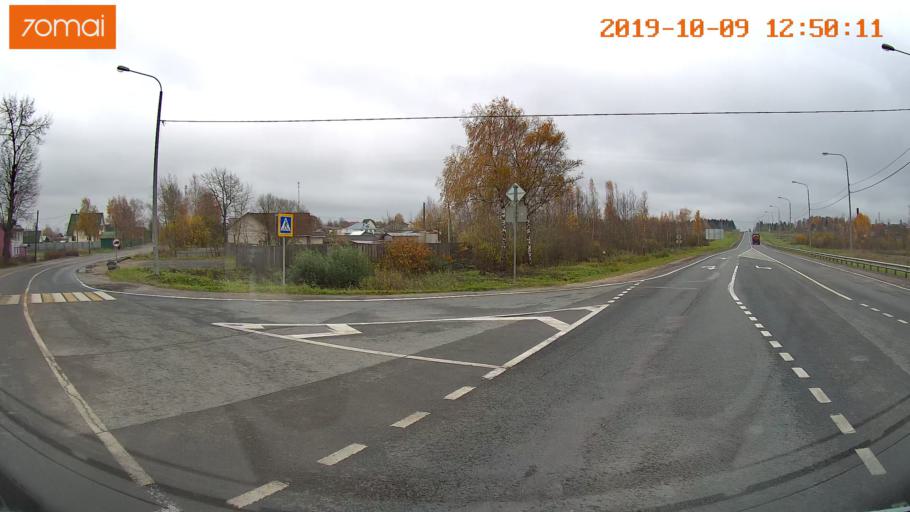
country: RU
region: Jaroslavl
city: Prechistoye
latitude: 58.4227
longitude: 40.3331
